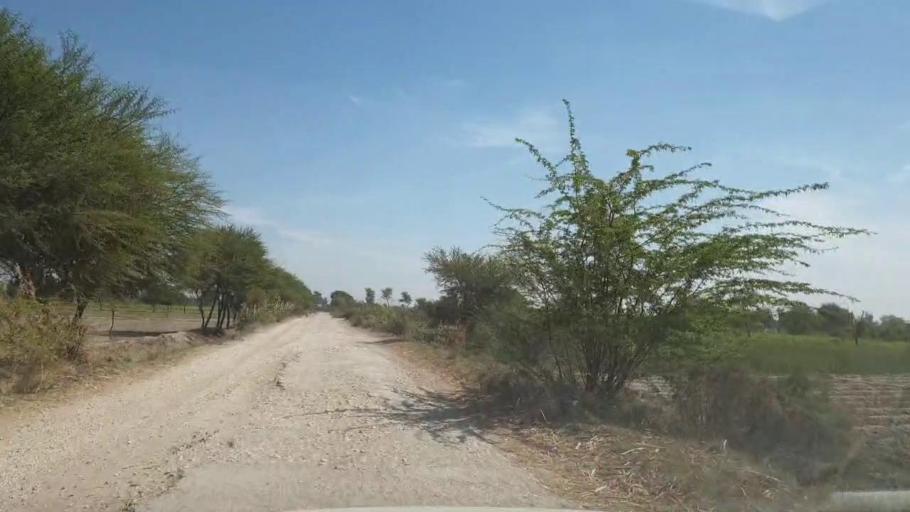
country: PK
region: Sindh
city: Pithoro
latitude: 25.6058
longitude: 69.2062
